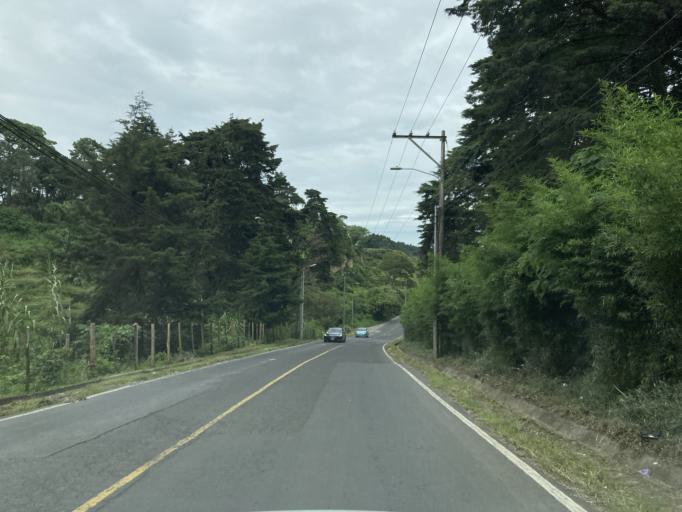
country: GT
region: Guatemala
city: San Jose Pinula
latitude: 14.5270
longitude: -90.4112
